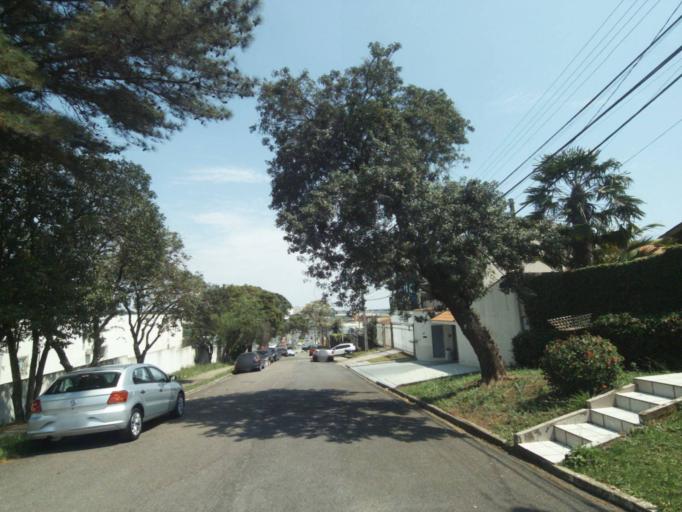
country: BR
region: Parana
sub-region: Curitiba
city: Curitiba
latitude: -25.4781
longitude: -49.3137
